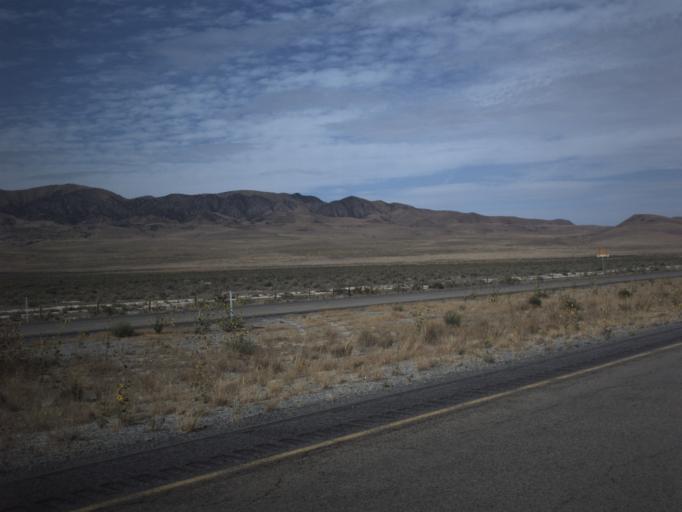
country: US
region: Utah
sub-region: Tooele County
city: Grantsville
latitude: 40.7773
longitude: -112.8074
